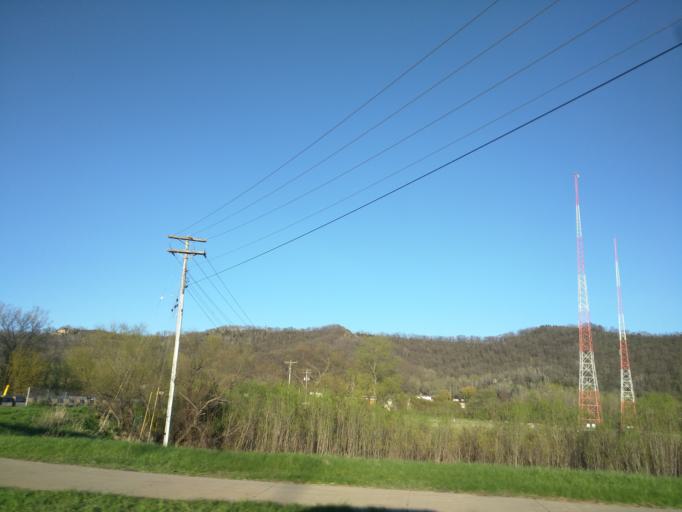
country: US
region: Wisconsin
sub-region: La Crosse County
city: North La Crosse
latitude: 43.8477
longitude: -91.2213
